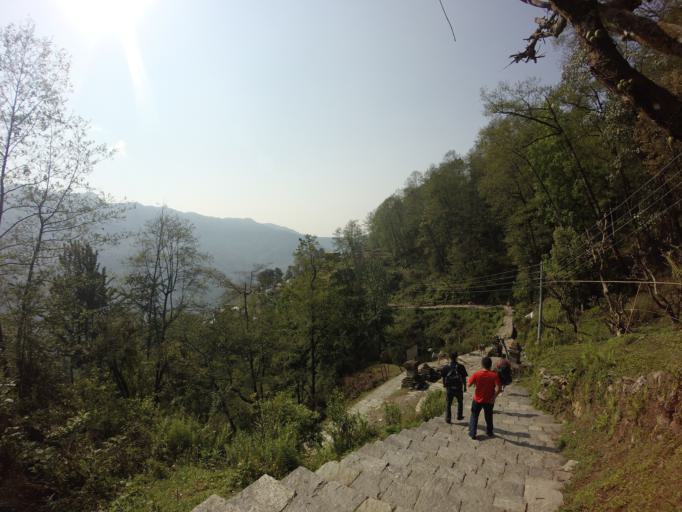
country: NP
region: Western Region
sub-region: Dhawalagiri Zone
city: Chitre
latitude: 28.3744
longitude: 83.8083
